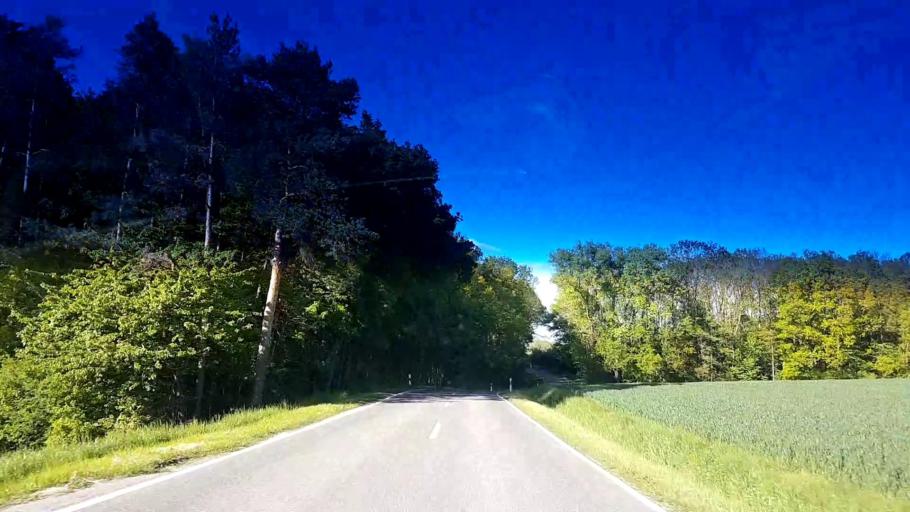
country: DE
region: Bavaria
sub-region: Upper Franconia
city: Zapfendorf
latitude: 49.9932
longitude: 10.9607
